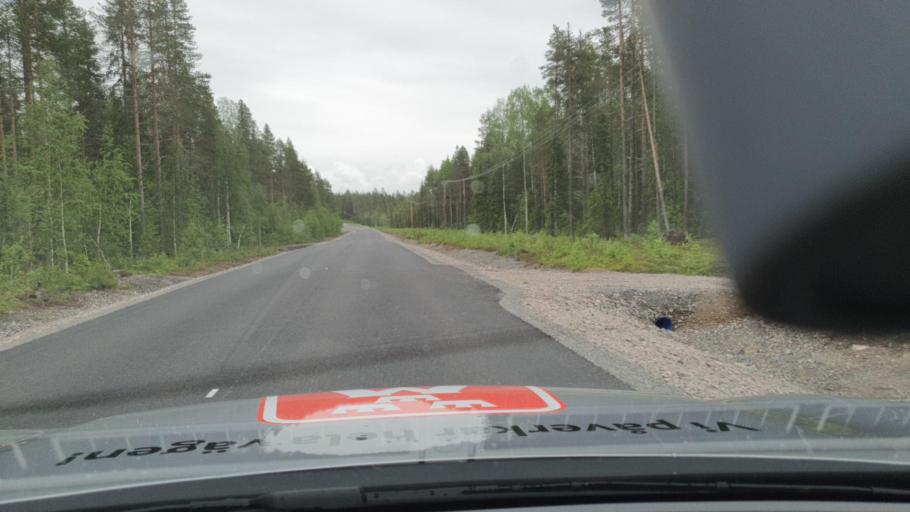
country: SE
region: Norrbotten
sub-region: Overtornea Kommun
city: OEvertornea
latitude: 66.6460
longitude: 23.2425
